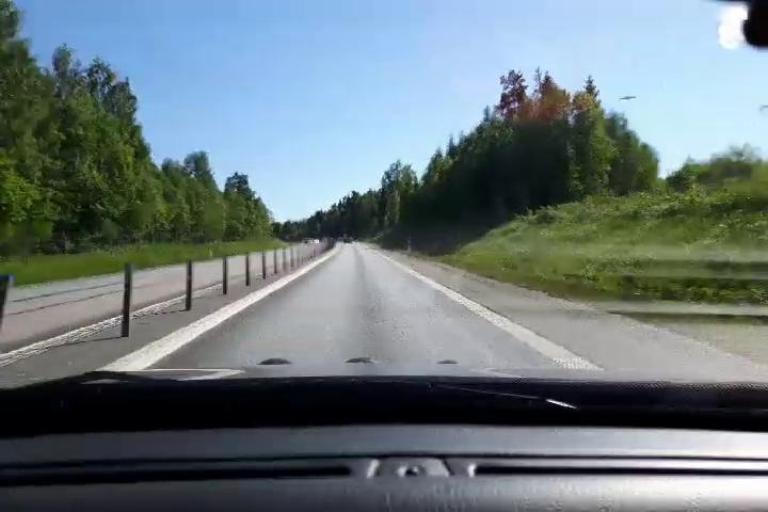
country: SE
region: Gaevleborg
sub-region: Gavle Kommun
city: Norrsundet
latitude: 60.9319
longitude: 17.0116
